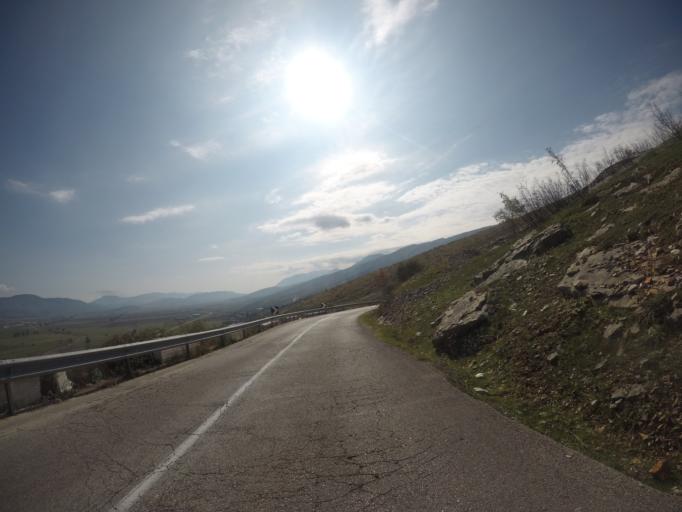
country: AL
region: Gjirokaster
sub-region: Rrethi i Gjirokastres
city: Libohove
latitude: 39.9457
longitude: 20.2565
